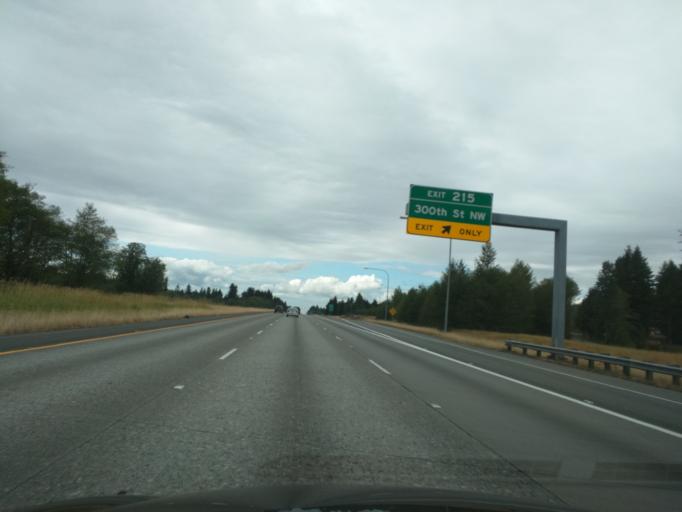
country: US
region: Washington
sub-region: Snohomish County
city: Stanwood
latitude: 48.2652
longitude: -122.2655
